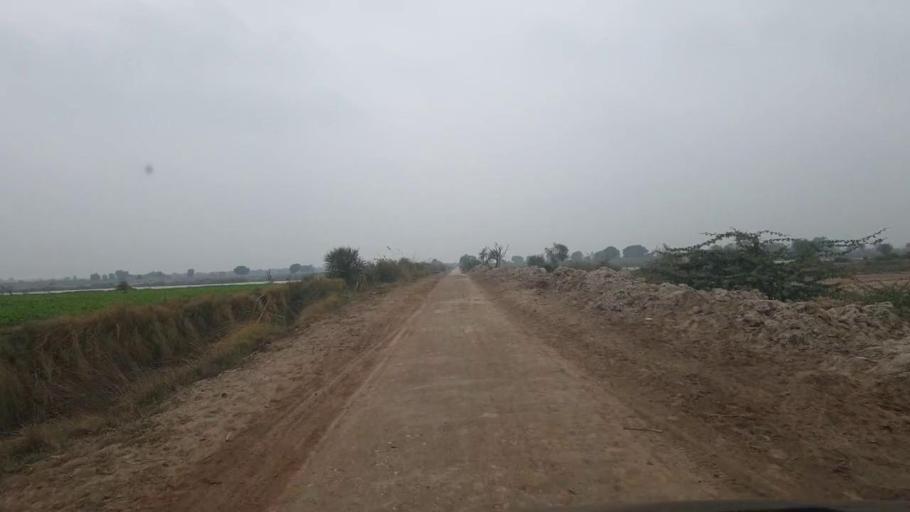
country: PK
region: Sindh
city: Tando Adam
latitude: 25.8436
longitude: 68.6821
